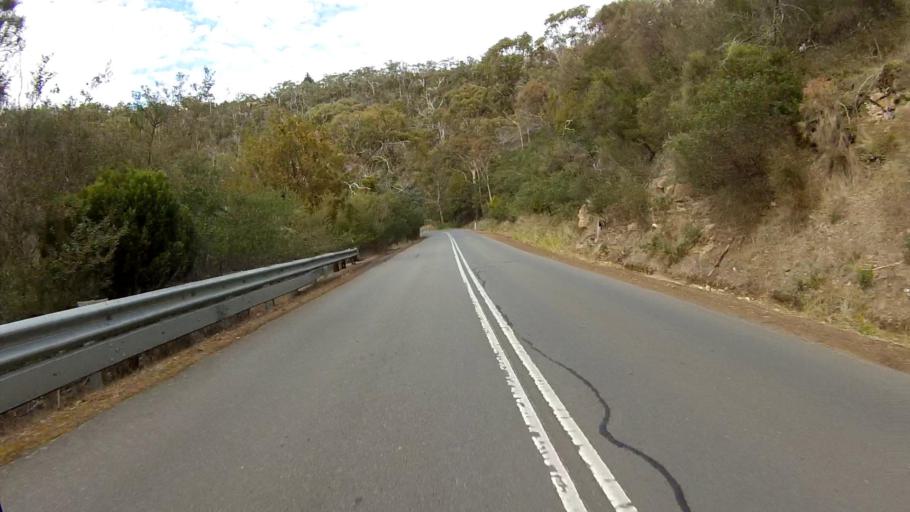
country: AU
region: Tasmania
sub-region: Clarence
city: Lindisfarne
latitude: -42.7800
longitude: 147.3701
